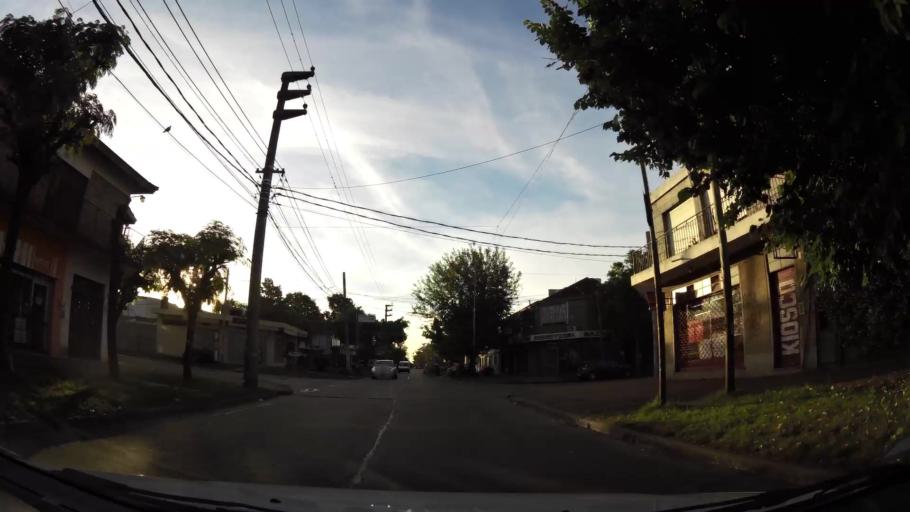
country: AR
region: Buenos Aires
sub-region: Partido de Moron
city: Moron
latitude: -34.6431
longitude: -58.6394
